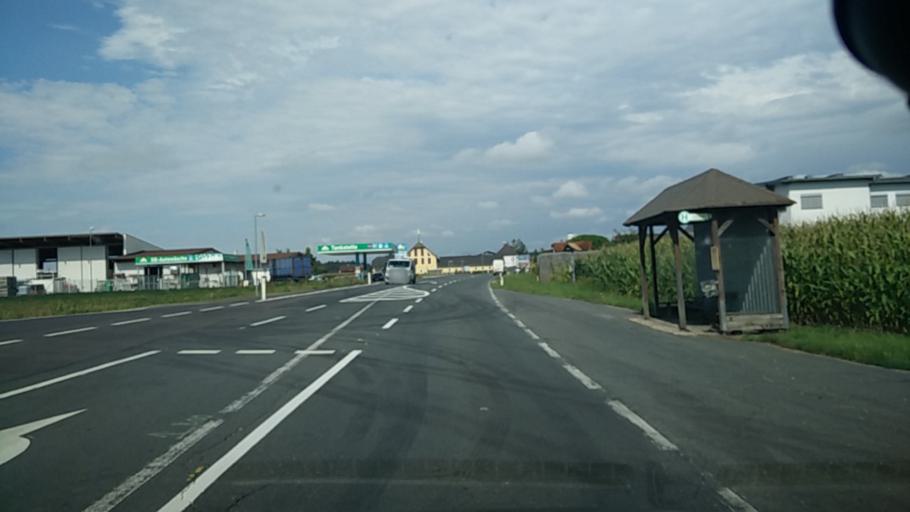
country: AT
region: Carinthia
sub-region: Politischer Bezirk Klagenfurt Land
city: Grafenstein
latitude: 46.6217
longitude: 14.4509
